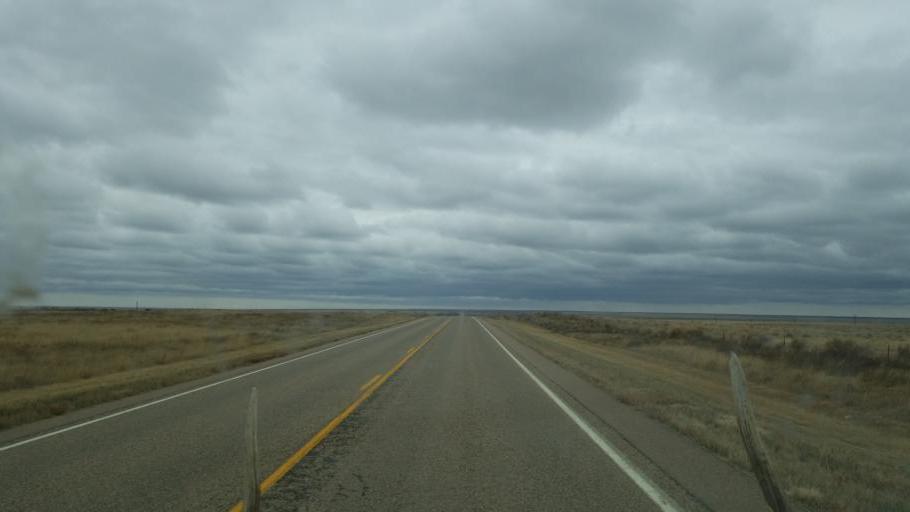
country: US
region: Colorado
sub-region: Kiowa County
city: Eads
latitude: 38.7762
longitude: -102.7389
